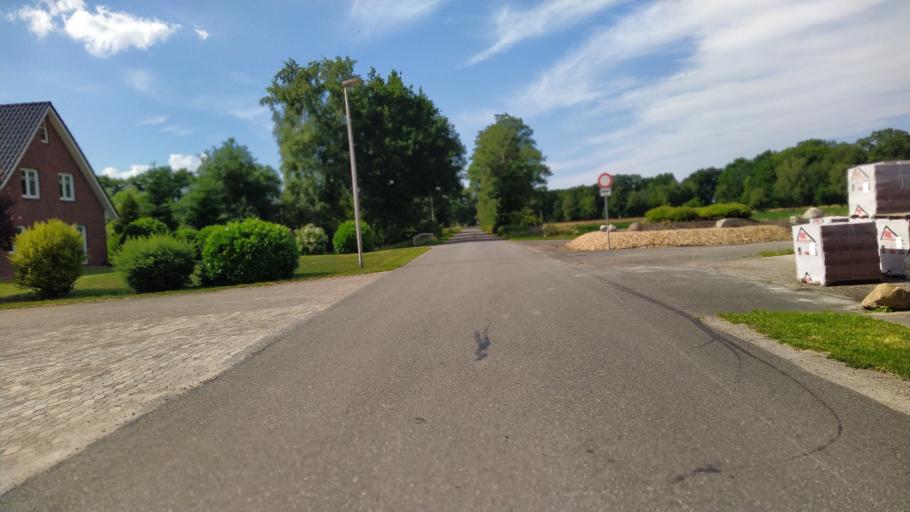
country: DE
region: Lower Saxony
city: Odisheim
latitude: 53.6522
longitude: 8.9376
